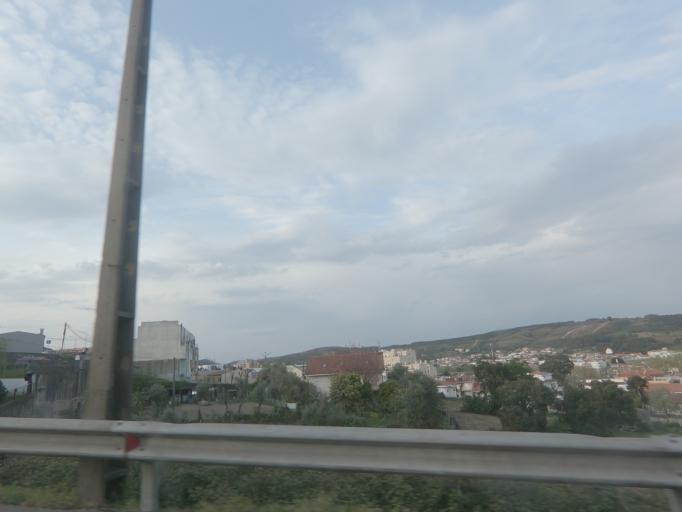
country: PT
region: Porto
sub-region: Valongo
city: Valongo
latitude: 41.1916
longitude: -8.5077
